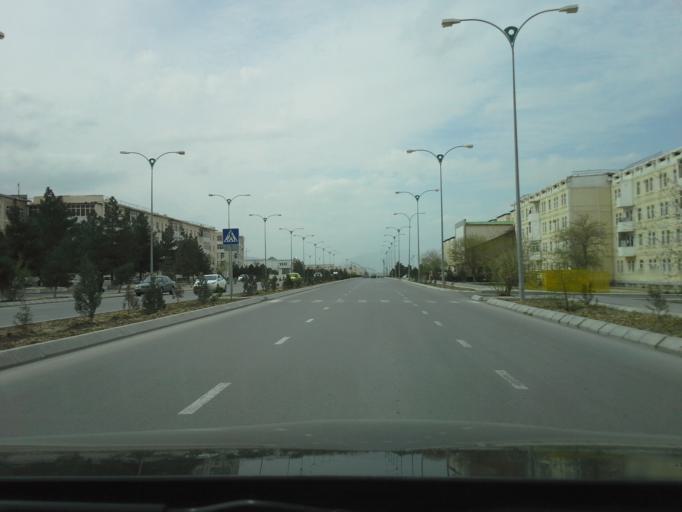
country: TM
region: Ahal
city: Abadan
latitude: 38.0544
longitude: 58.1533
